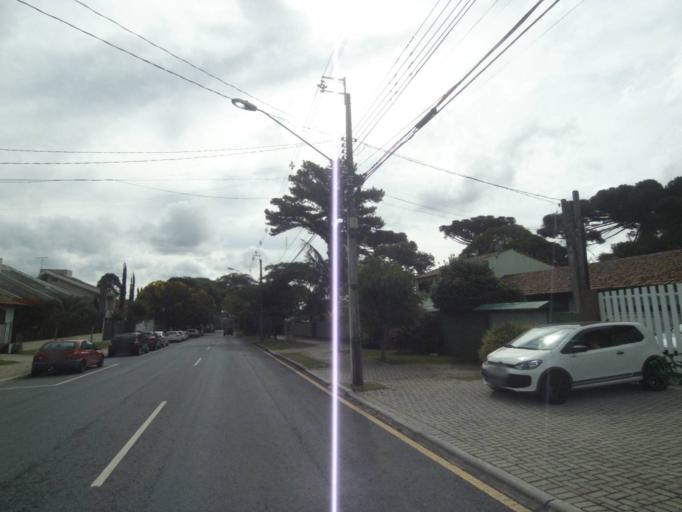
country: BR
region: Parana
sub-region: Curitiba
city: Curitiba
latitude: -25.4412
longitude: -49.3005
